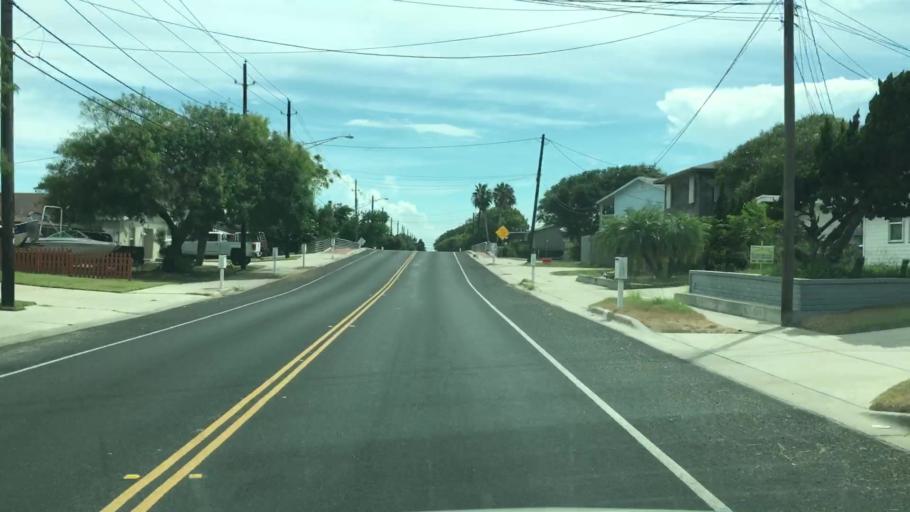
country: US
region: Texas
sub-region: Nueces County
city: Corpus Christi
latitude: 27.6286
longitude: -97.2921
